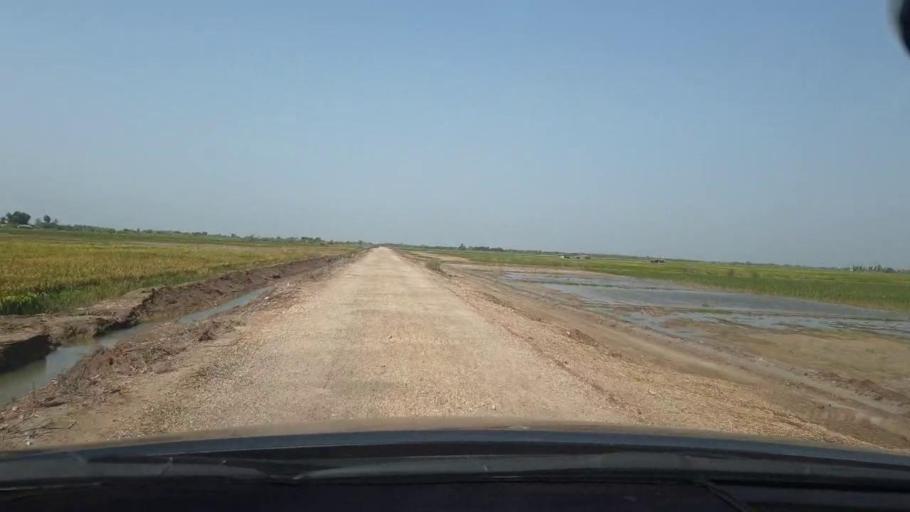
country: PK
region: Sindh
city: Tando Bago
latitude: 24.7179
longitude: 69.1153
